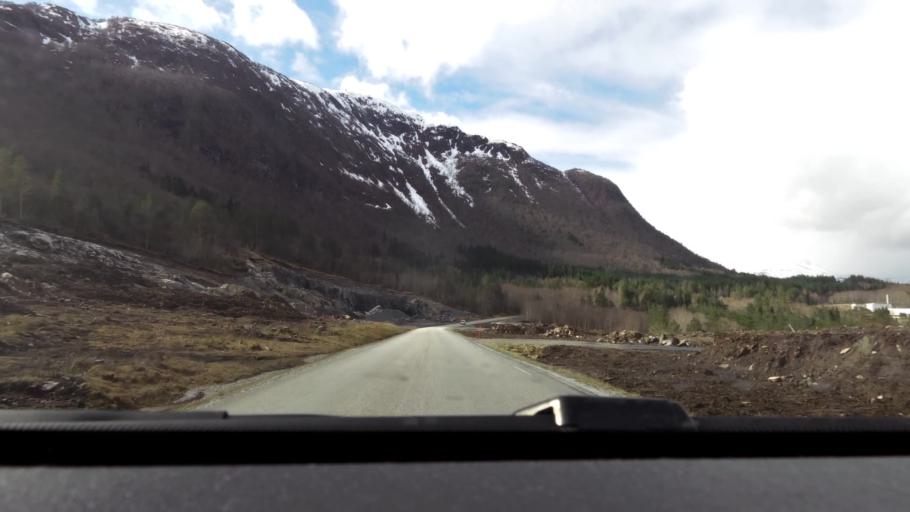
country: NO
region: More og Romsdal
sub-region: Averoy
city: Bruhagen
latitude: 63.0979
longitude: 7.6282
